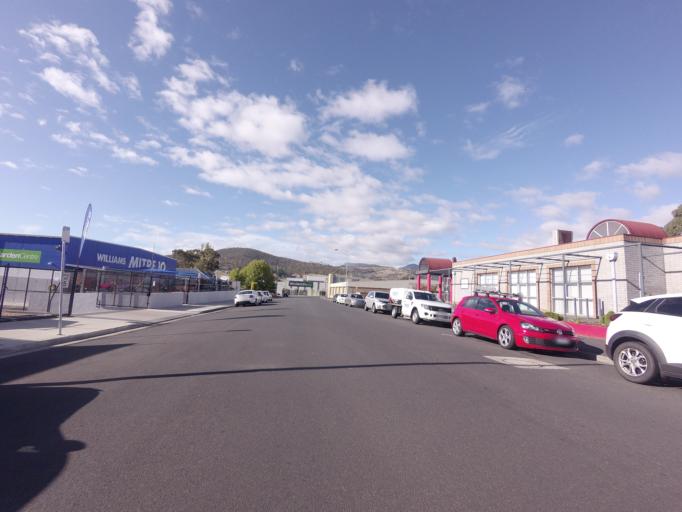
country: AU
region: Tasmania
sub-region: Derwent Valley
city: New Norfolk
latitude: -42.7812
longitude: 147.0642
